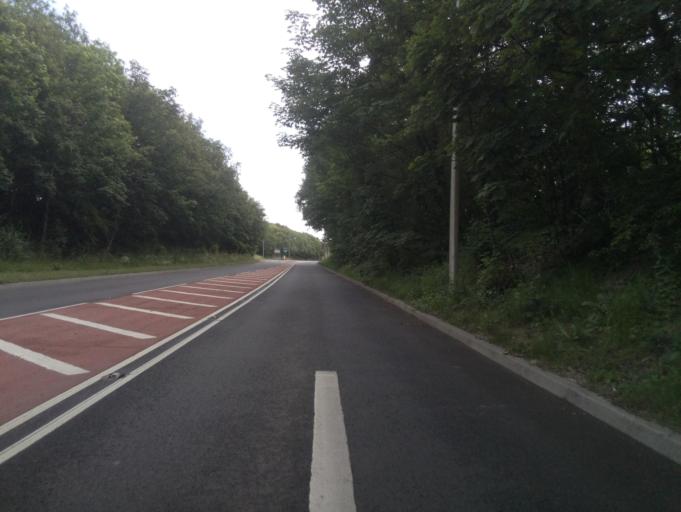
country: GB
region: Wales
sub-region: Vale of Glamorgan
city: Llantwit Major
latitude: 51.4061
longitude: -3.4576
